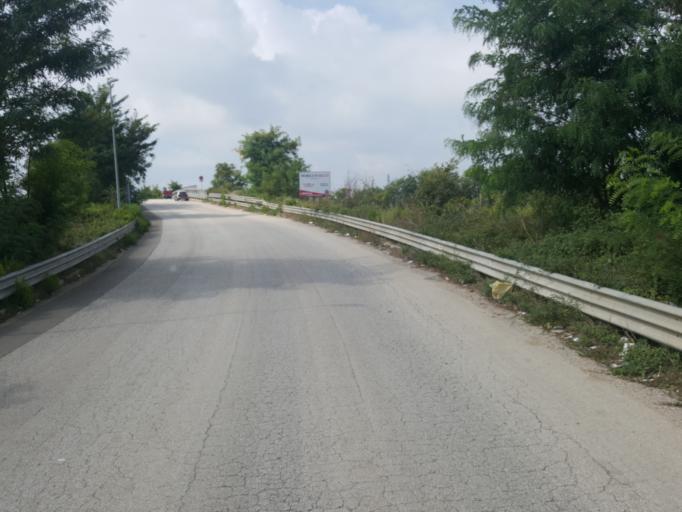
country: IT
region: Campania
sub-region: Provincia di Caserta
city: Pignataro Maggiore
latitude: 41.1799
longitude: 14.1558
